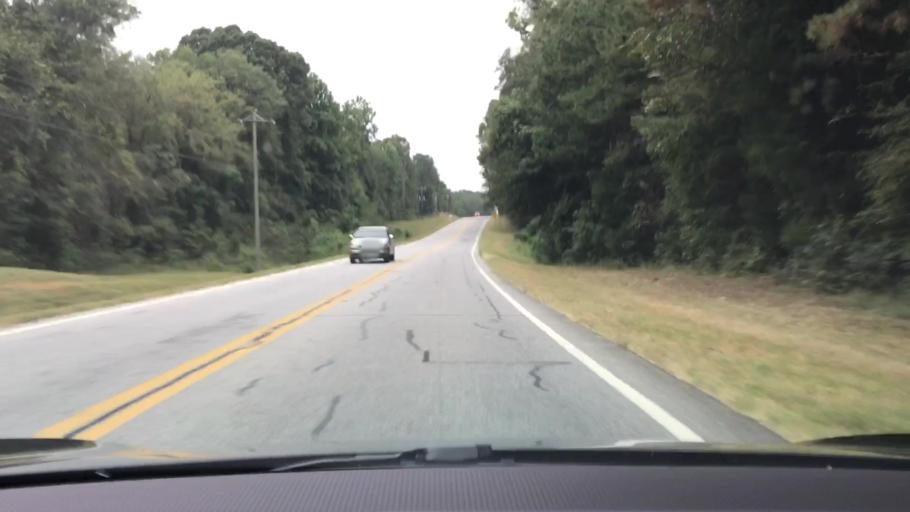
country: US
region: Georgia
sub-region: Oconee County
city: Watkinsville
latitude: 33.7628
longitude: -83.3091
